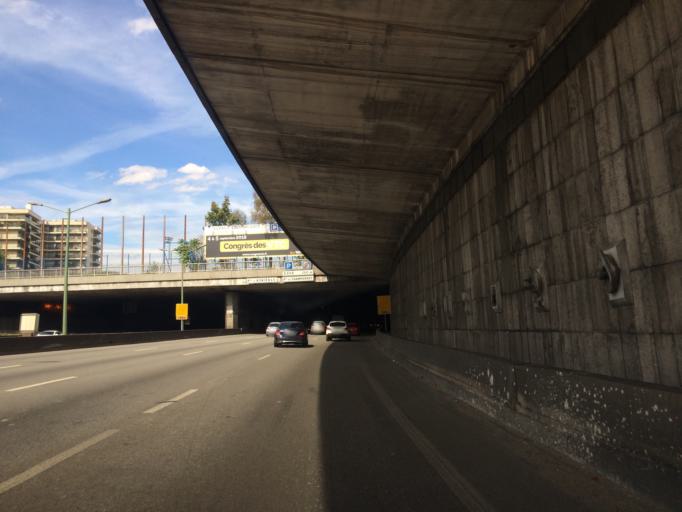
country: FR
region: Ile-de-France
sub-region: Departement des Hauts-de-Seine
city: Levallois-Perret
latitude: 48.8826
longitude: 2.2835
